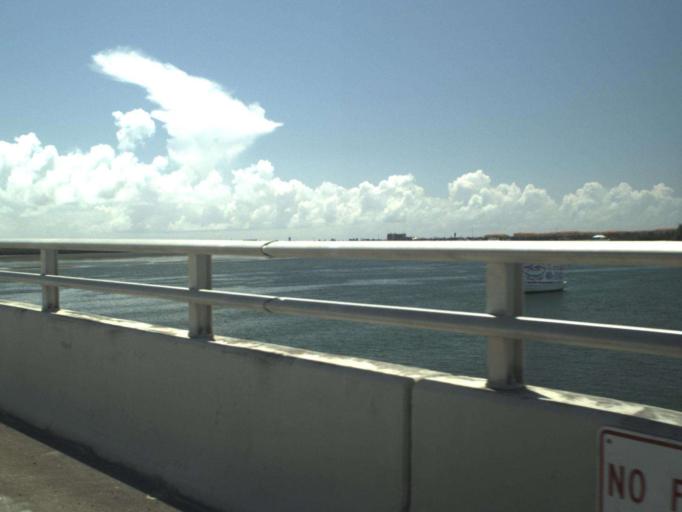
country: US
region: Florida
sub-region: Saint Lucie County
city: Fort Pierce
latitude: 27.4714
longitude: -80.3261
